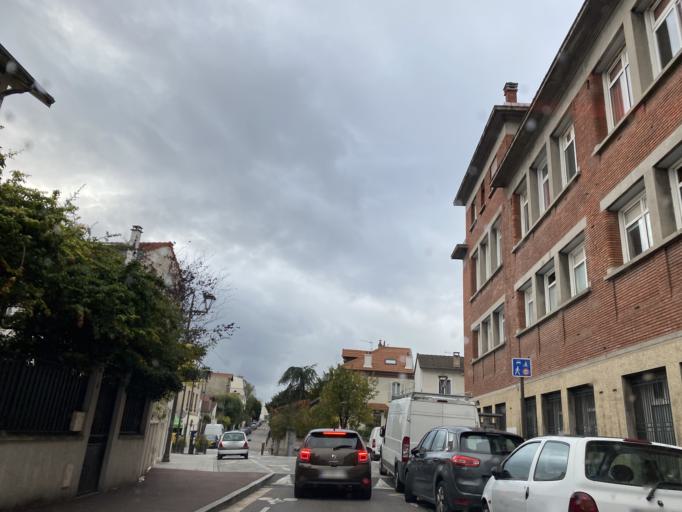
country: FR
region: Ile-de-France
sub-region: Departement des Hauts-de-Seine
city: Suresnes
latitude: 48.8766
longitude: 2.2233
